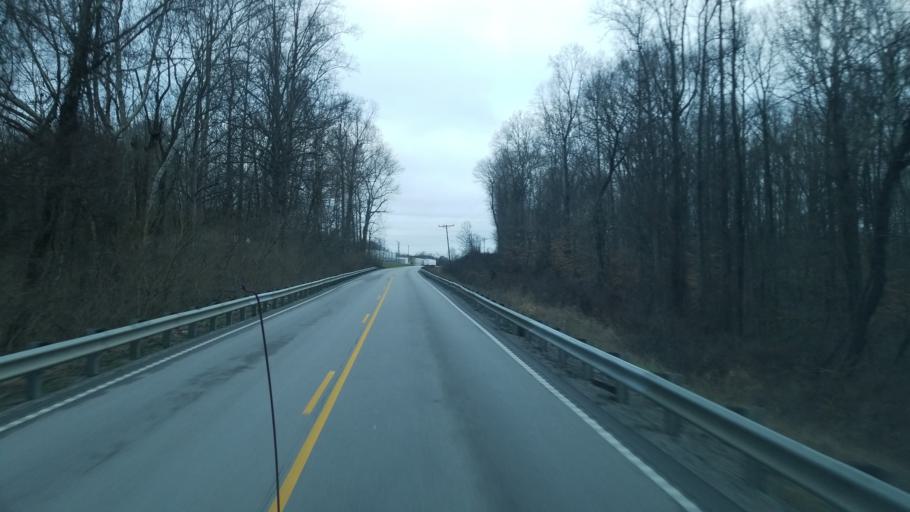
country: US
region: Ohio
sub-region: Brown County
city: Aberdeen
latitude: 38.6889
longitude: -83.7954
